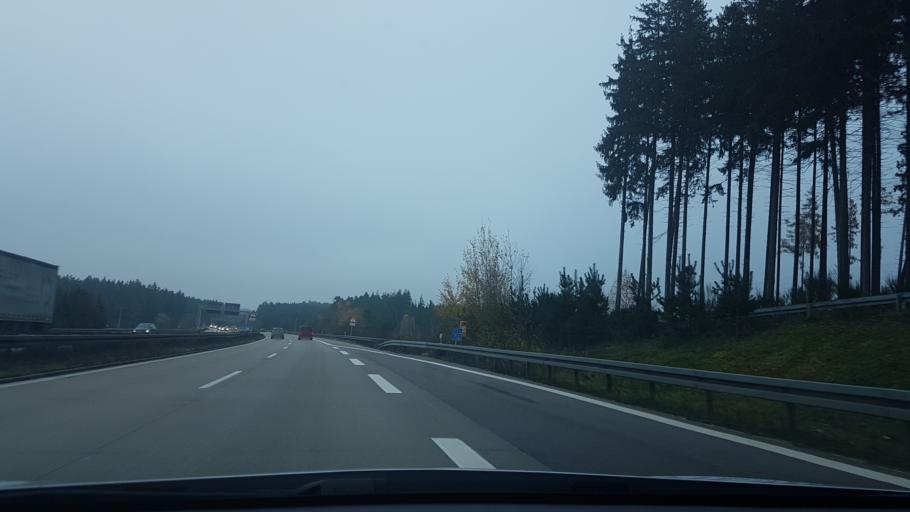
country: DE
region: Bavaria
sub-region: Lower Bavaria
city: Bad Abbach
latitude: 48.8925
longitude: 12.0771
